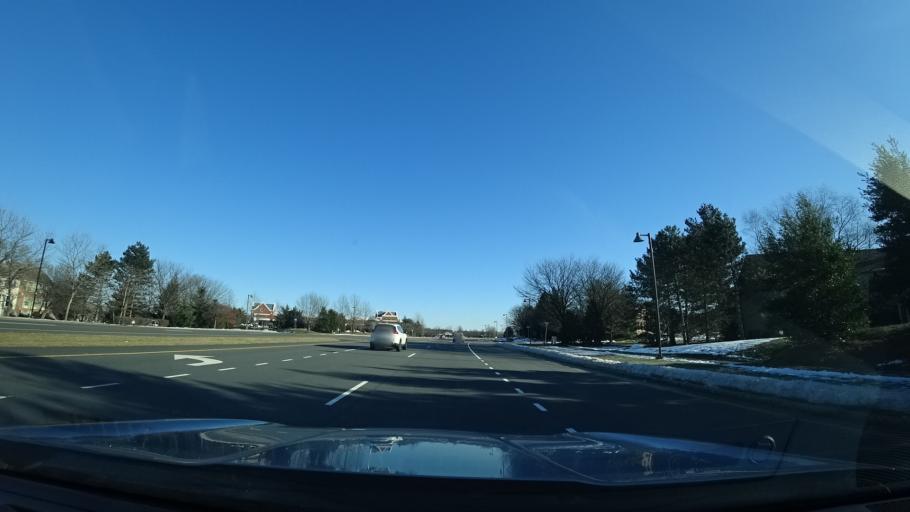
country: US
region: Virginia
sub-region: Loudoun County
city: Ashburn
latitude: 39.0449
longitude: -77.4792
